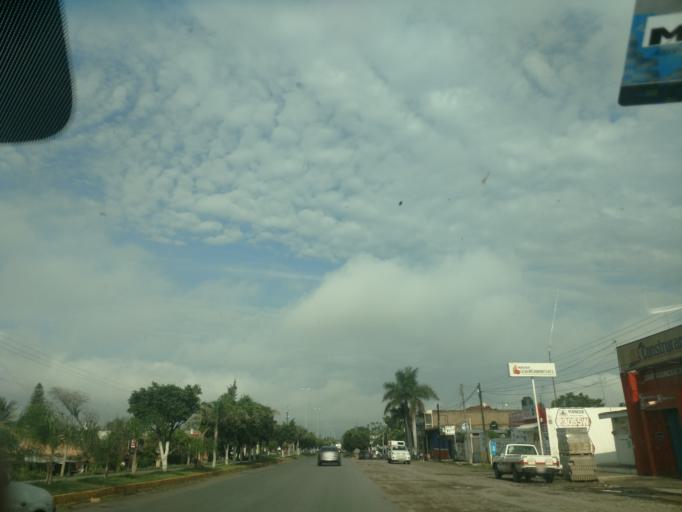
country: MX
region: Jalisco
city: Ameca
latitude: 20.5363
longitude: -104.0324
